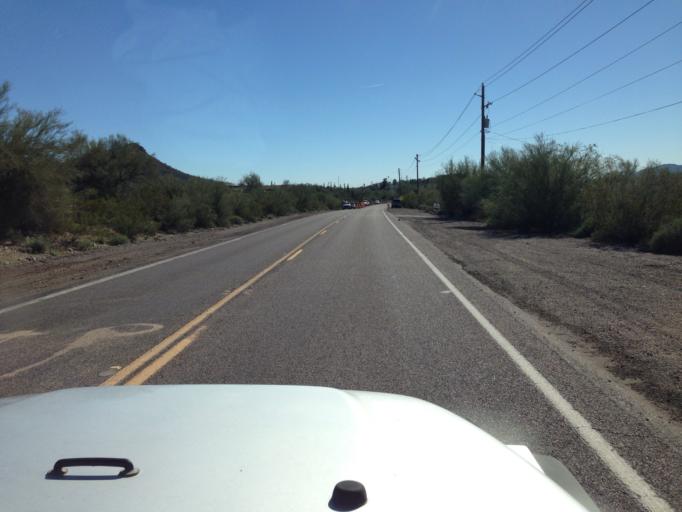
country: US
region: Arizona
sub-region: Maricopa County
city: New River
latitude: 33.8988
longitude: -112.0776
